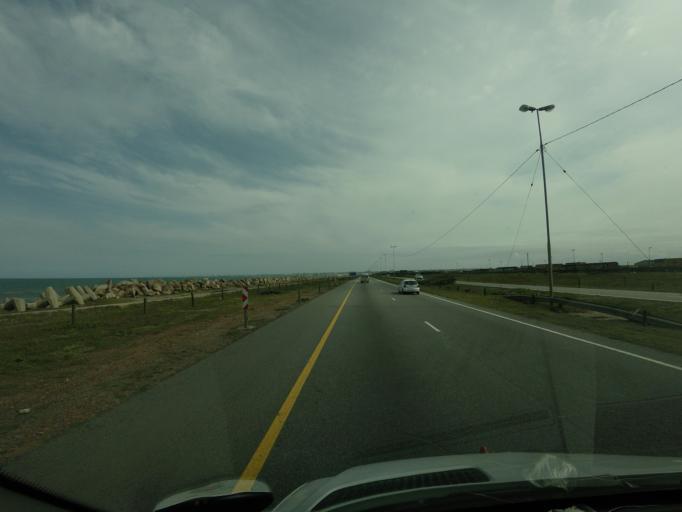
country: ZA
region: Eastern Cape
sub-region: Nelson Mandela Bay Metropolitan Municipality
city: Port Elizabeth
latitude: -33.8934
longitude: 25.6216
